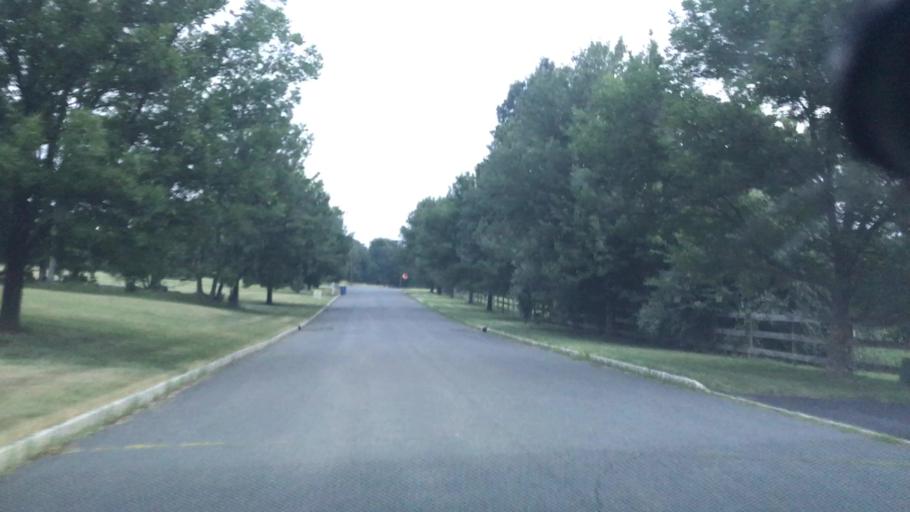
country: US
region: New Jersey
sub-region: Hunterdon County
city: Lebanon
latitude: 40.6690
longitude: -74.8387
